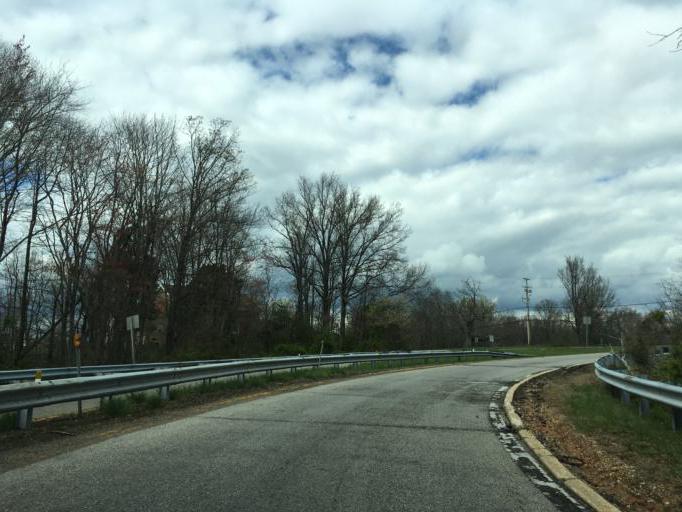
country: US
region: Maryland
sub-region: Anne Arundel County
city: Jessup
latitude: 39.1399
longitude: -76.7573
